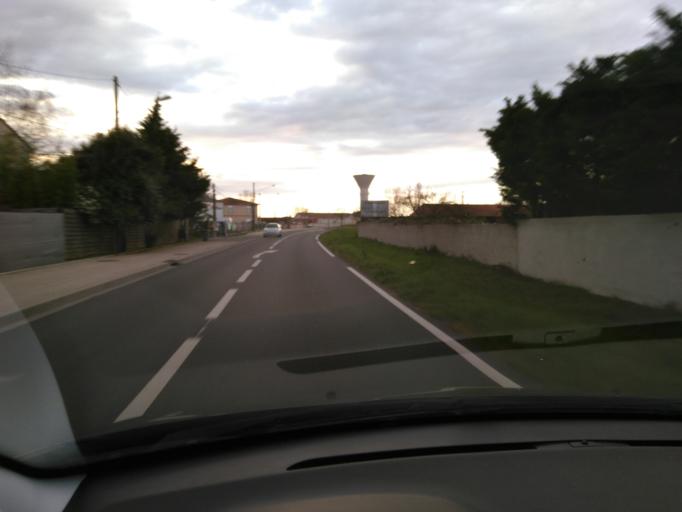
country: FR
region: Midi-Pyrenees
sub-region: Departement de la Haute-Garonne
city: Pibrac
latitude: 43.6090
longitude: 1.2662
